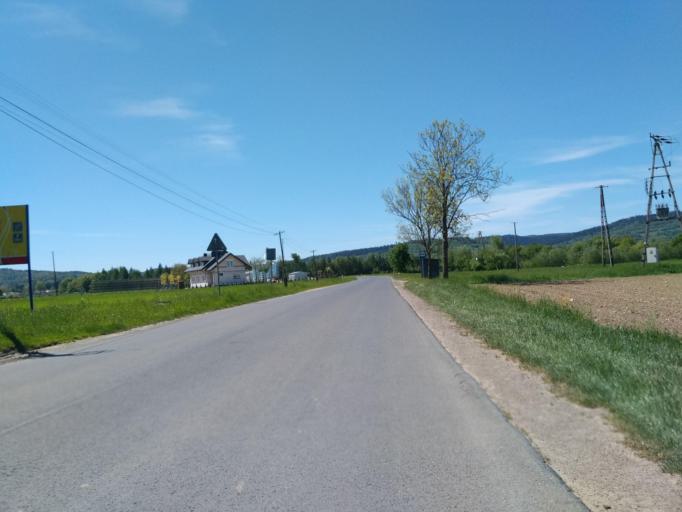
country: PL
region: Subcarpathian Voivodeship
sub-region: Powiat krosnienski
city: Sieniawa
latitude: 49.5597
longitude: 21.9376
